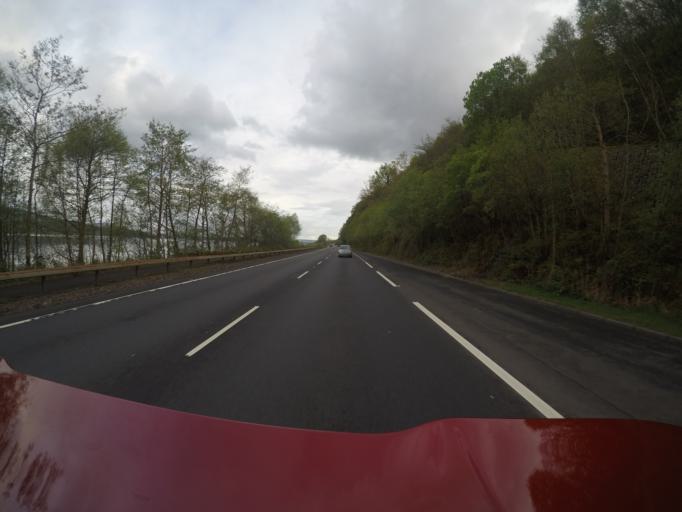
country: GB
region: Scotland
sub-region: Argyll and Bute
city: Helensburgh
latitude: 56.1357
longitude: -4.6587
